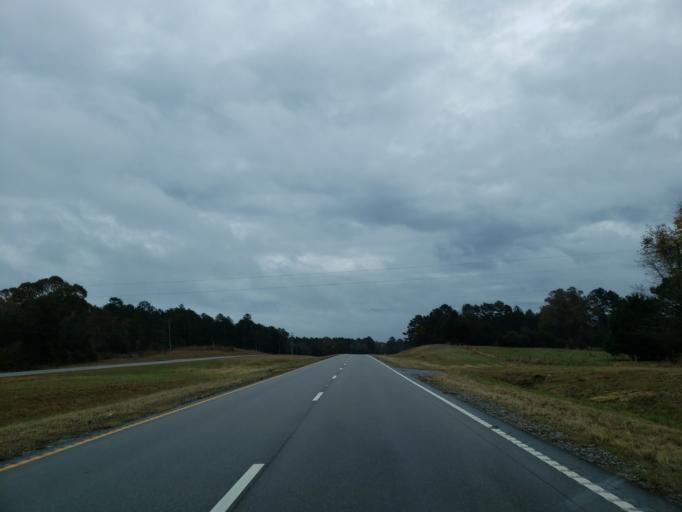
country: US
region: Mississippi
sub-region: Wayne County
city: Waynesboro
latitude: 31.6958
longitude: -88.7289
